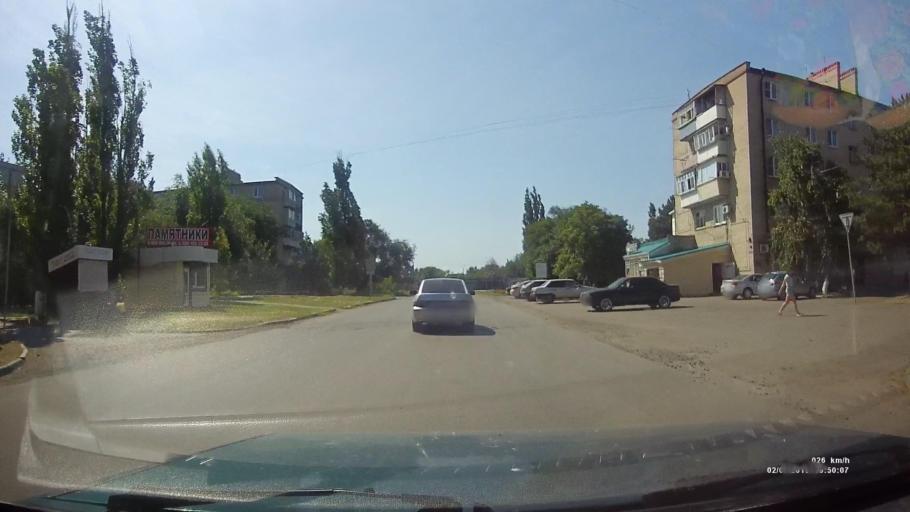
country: RU
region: Rostov
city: Azov
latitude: 47.1025
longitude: 39.4030
